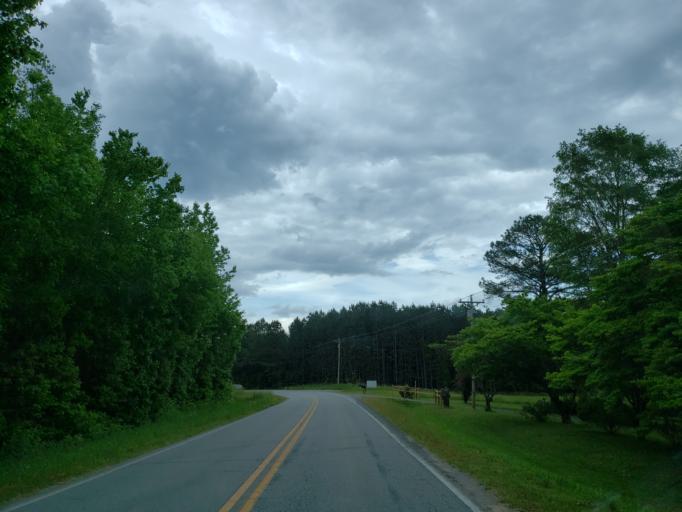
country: US
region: Georgia
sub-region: Polk County
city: Rockmart
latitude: 33.9050
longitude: -85.0664
